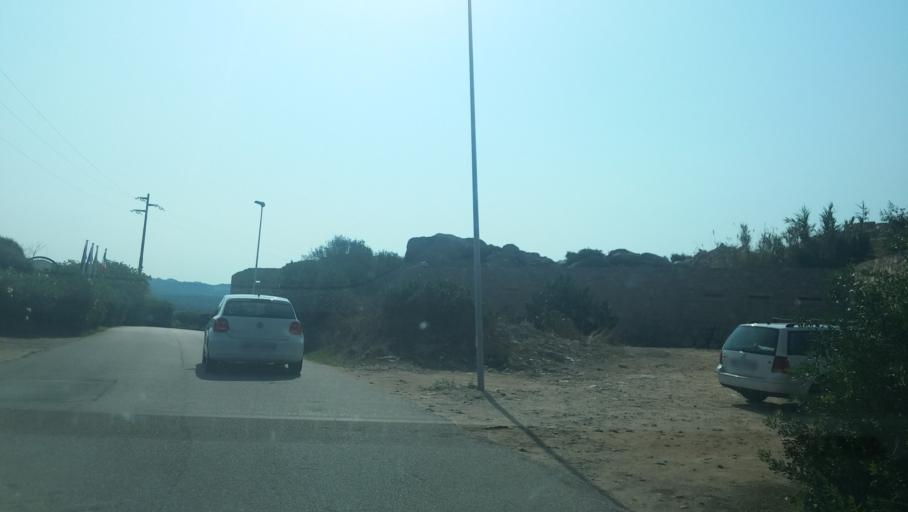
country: IT
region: Sardinia
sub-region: Provincia di Olbia-Tempio
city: La Maddalena
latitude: 41.2179
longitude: 9.4382
